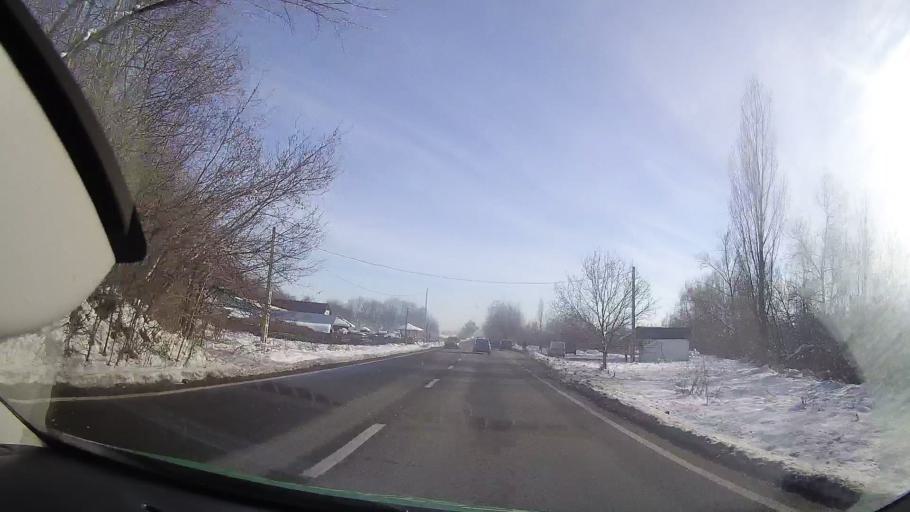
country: RO
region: Neamt
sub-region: Comuna Negresti
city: Negresti
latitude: 47.0704
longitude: 26.3652
